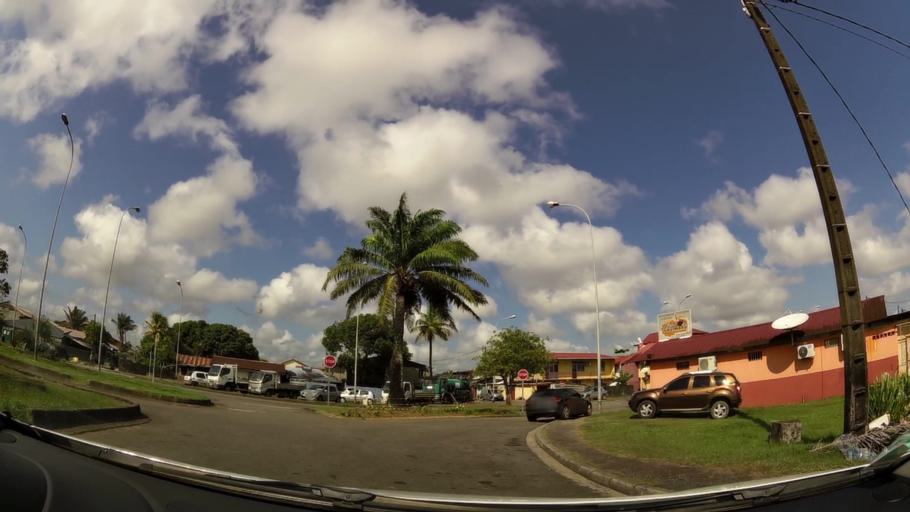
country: GF
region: Guyane
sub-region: Guyane
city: Cayenne
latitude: 4.9358
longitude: -52.3193
